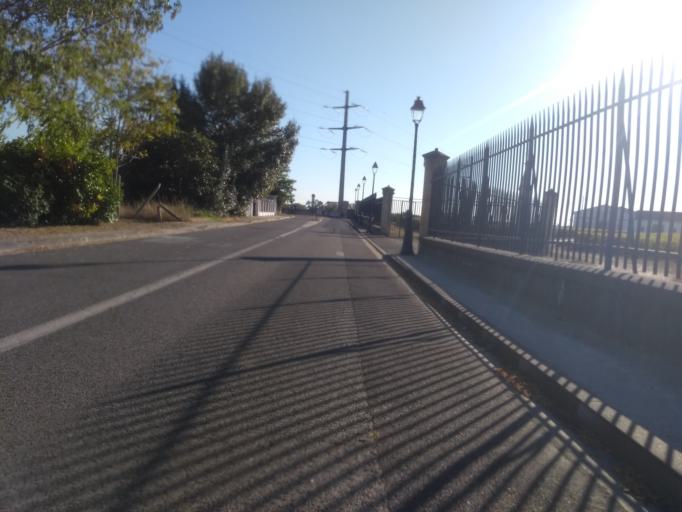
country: FR
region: Aquitaine
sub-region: Departement de la Gironde
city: Talence
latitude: 44.8162
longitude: -0.6032
